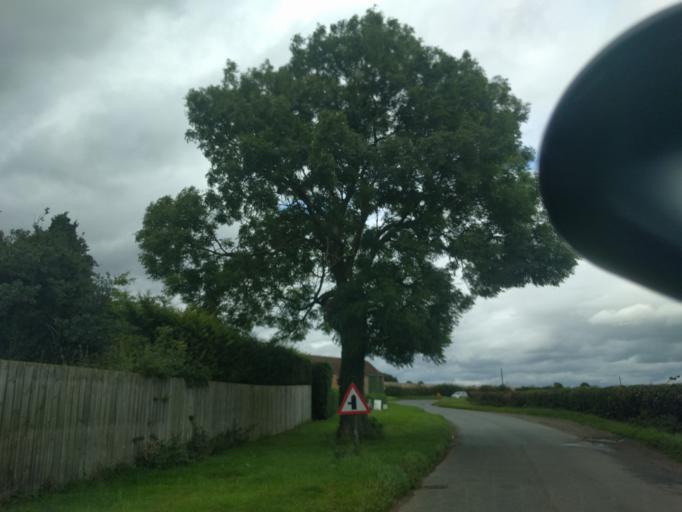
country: GB
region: England
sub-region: North Yorkshire
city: Bedale
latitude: 54.3140
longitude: -1.5638
